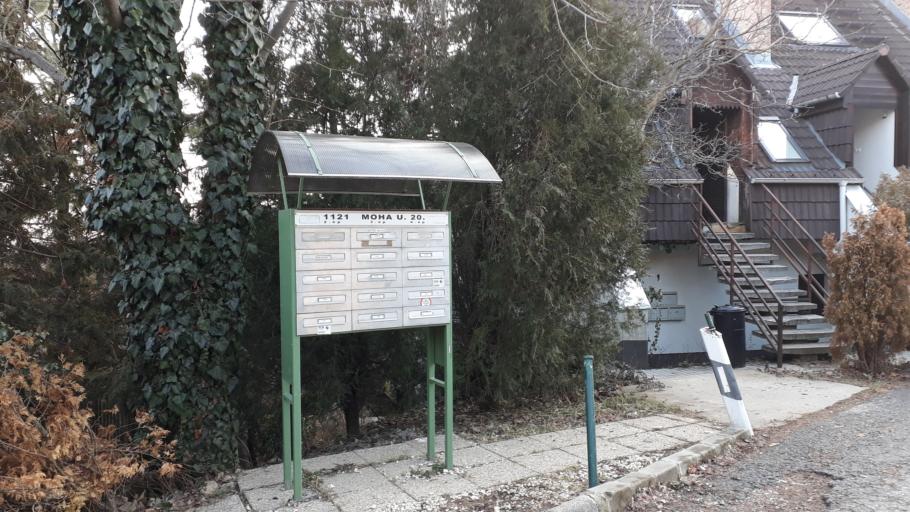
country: HU
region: Pest
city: Budaors
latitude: 47.4839
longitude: 18.9747
